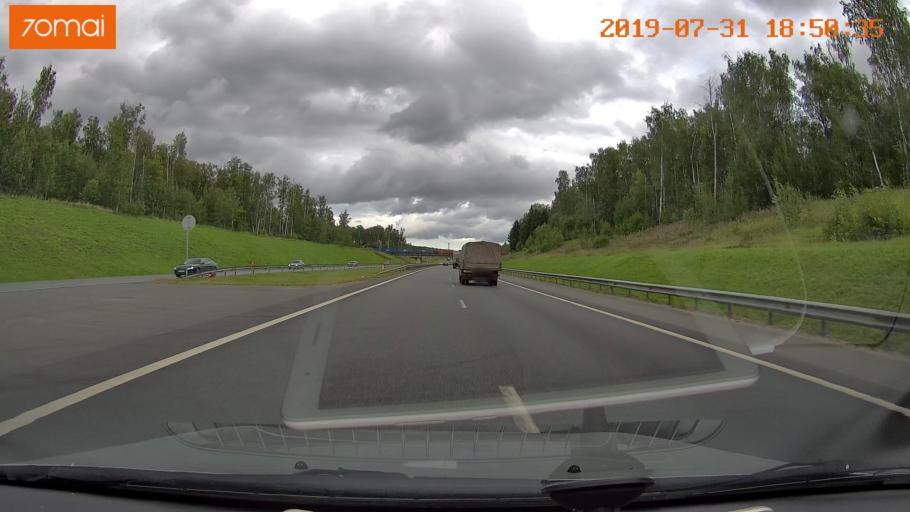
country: RU
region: Moskovskaya
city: Troitskoye
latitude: 55.2279
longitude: 38.5856
